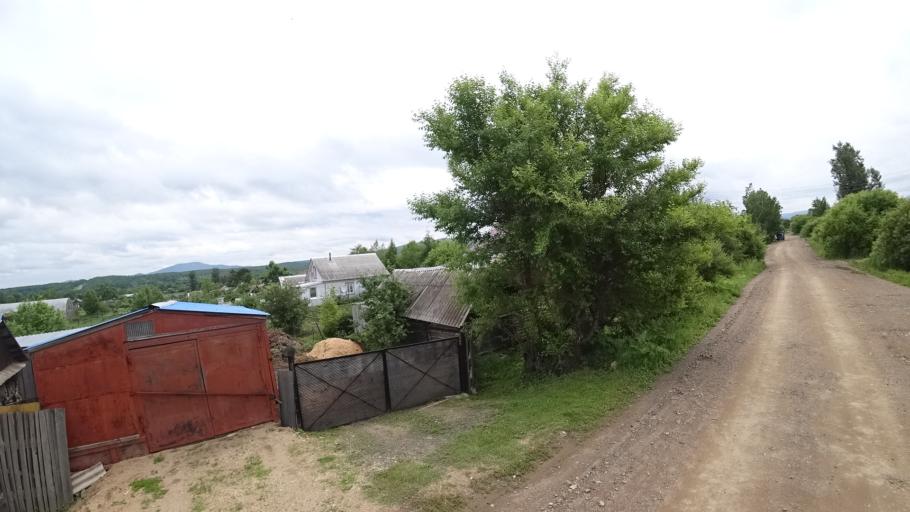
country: RU
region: Primorskiy
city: Novosysoyevka
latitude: 44.2293
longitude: 133.3668
